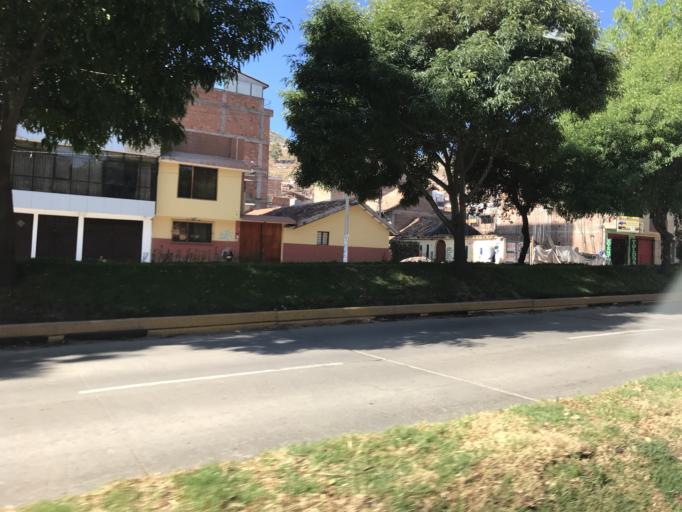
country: PE
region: Cusco
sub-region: Provincia de Cusco
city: Cusco
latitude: -13.5322
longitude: -71.9638
